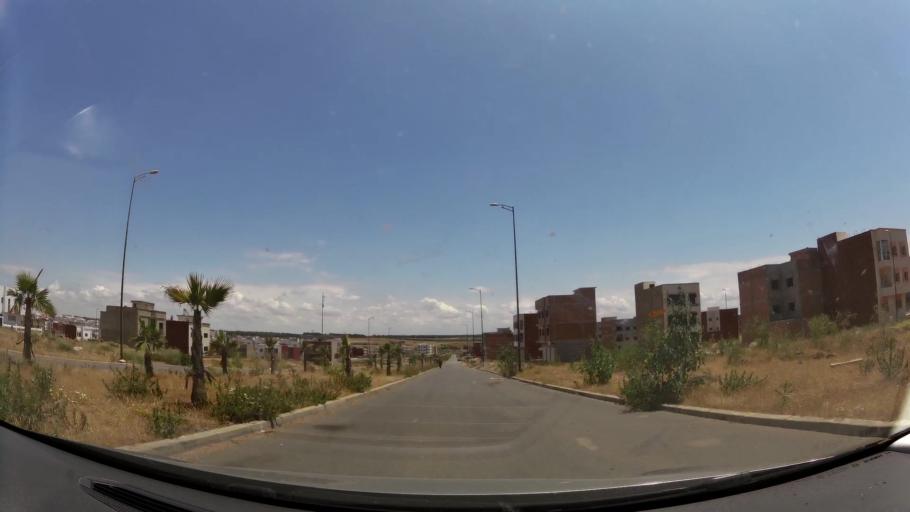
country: MA
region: Gharb-Chrarda-Beni Hssen
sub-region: Kenitra Province
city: Kenitra
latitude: 34.2481
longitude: -6.6598
